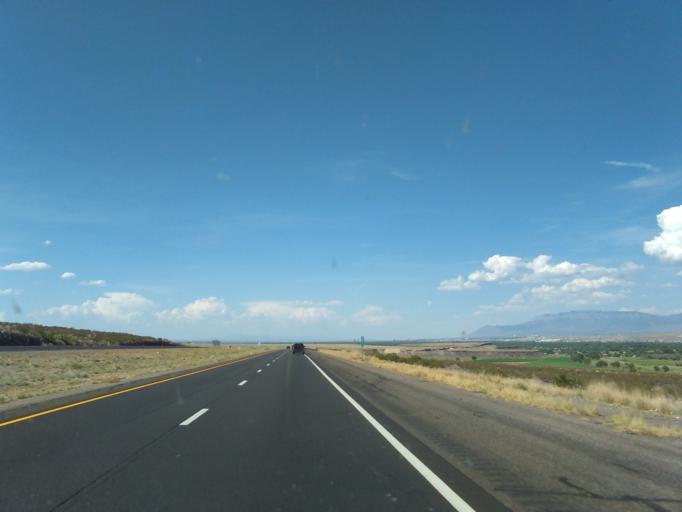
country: US
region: New Mexico
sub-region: Valencia County
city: Bosque Farms
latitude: 34.9197
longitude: -106.7197
